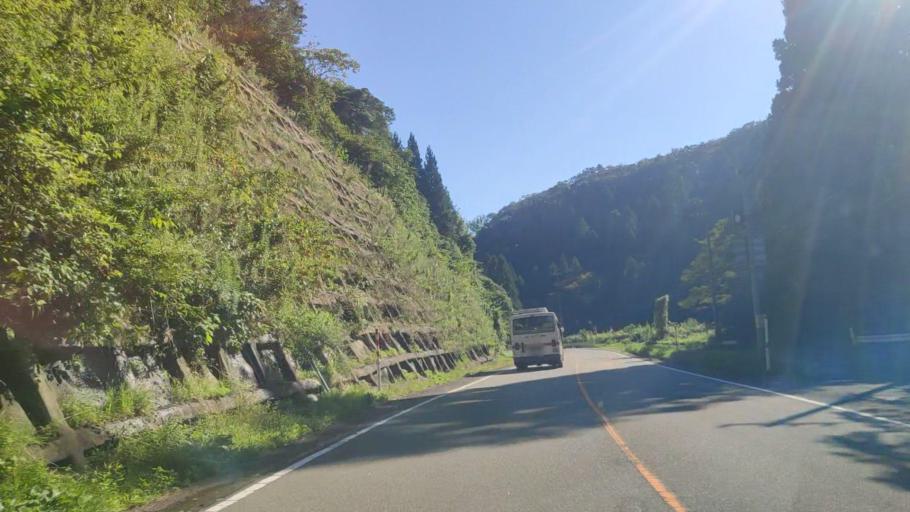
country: JP
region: Ishikawa
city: Nanao
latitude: 37.2403
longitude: 136.9795
